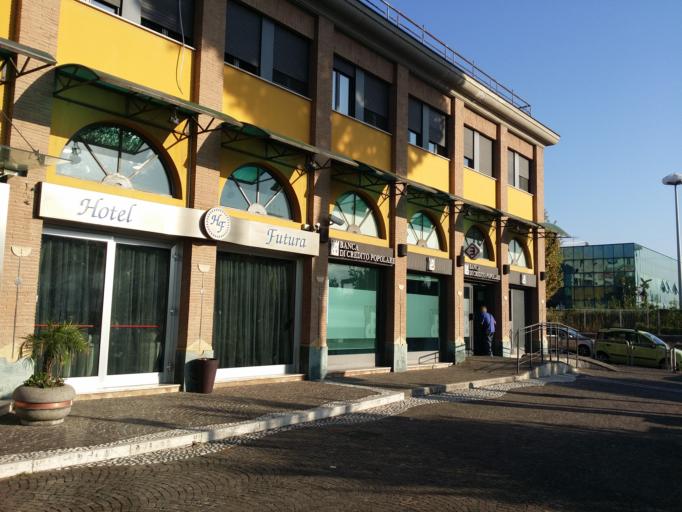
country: IT
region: Campania
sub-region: Provincia di Napoli
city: Arpino
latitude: 40.8906
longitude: 14.3228
